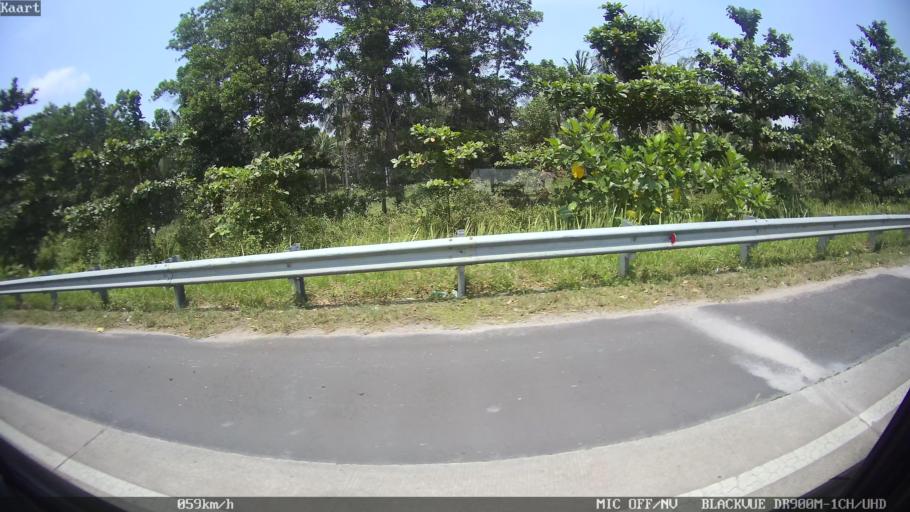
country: ID
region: Lampung
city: Kedaton
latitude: -5.3820
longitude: 105.3340
